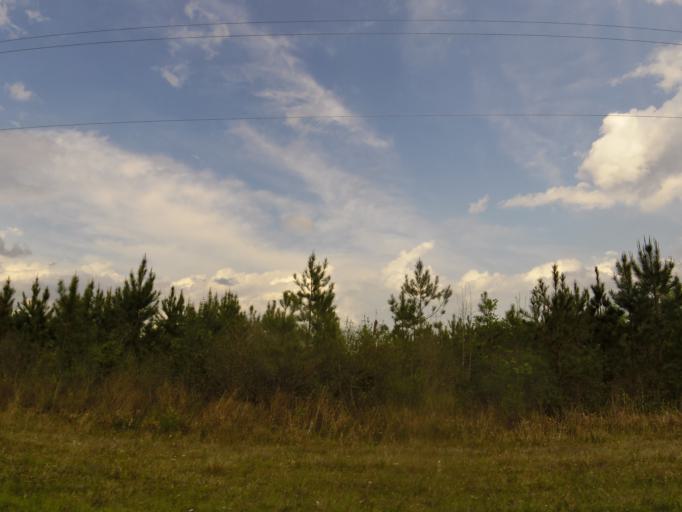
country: US
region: Georgia
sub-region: Charlton County
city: Folkston
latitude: 30.8150
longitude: -82.0699
